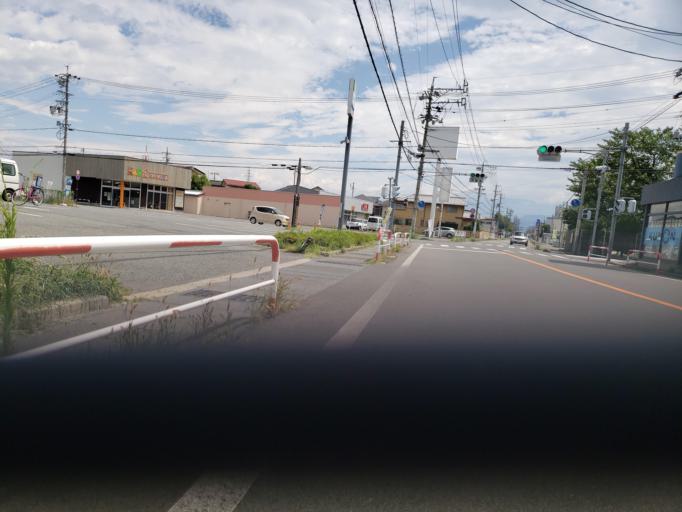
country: JP
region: Nagano
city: Nagano-shi
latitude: 36.6333
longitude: 138.1722
